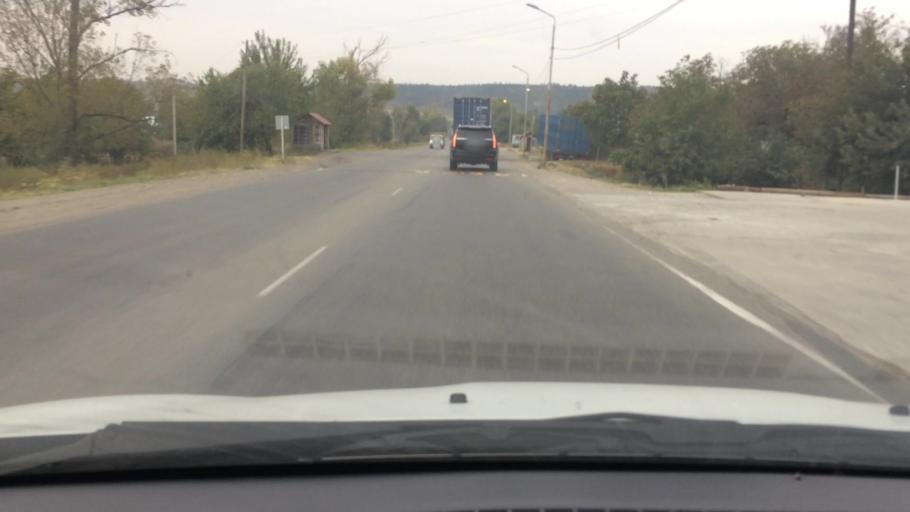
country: GE
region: T'bilisi
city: Tbilisi
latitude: 41.6133
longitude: 44.7892
